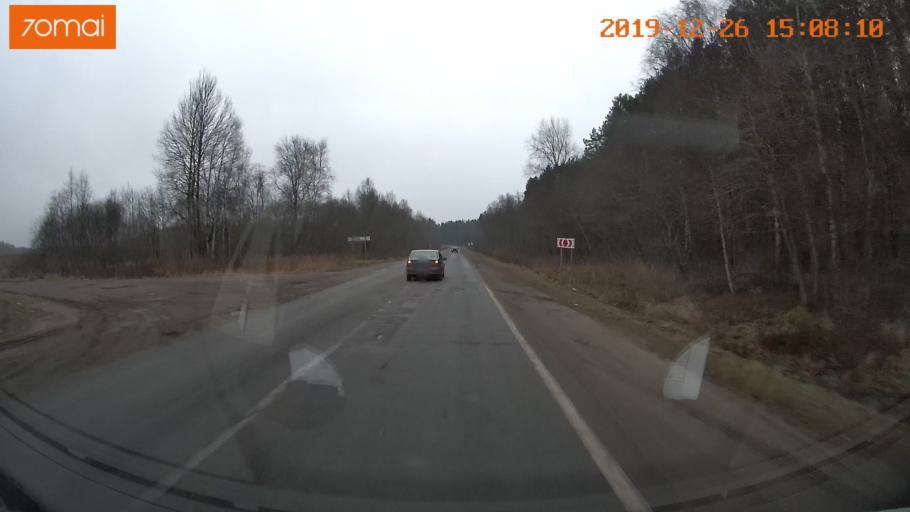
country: RU
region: Jaroslavl
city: Rybinsk
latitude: 58.1625
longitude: 38.8399
